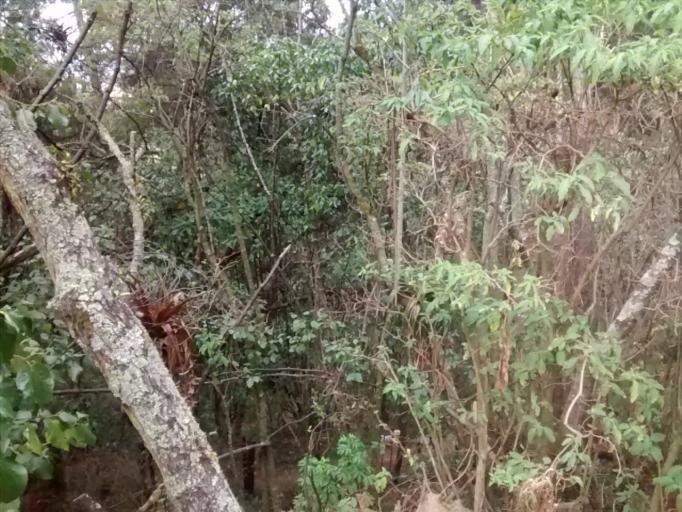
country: CO
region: Bogota D.C.
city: Bogota
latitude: 4.5988
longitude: -74.0614
